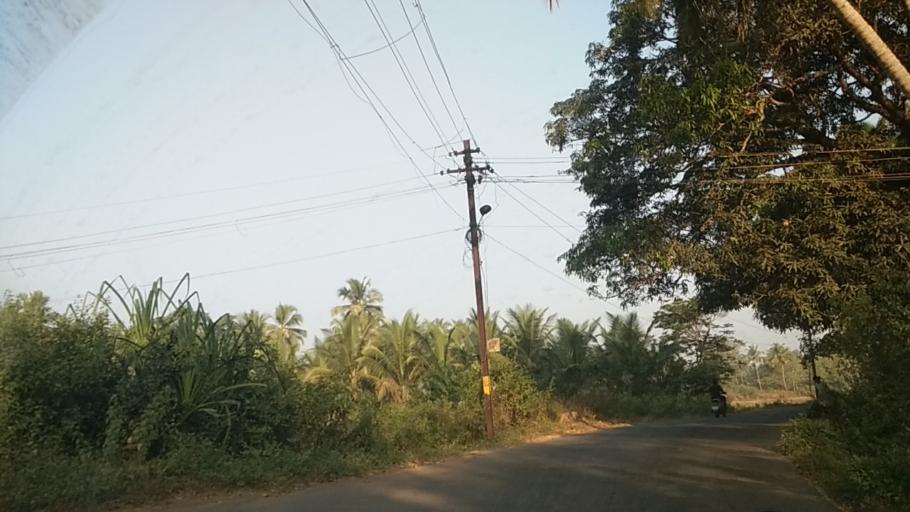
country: IN
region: Goa
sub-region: South Goa
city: Benaulim
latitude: 15.2706
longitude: 73.9383
